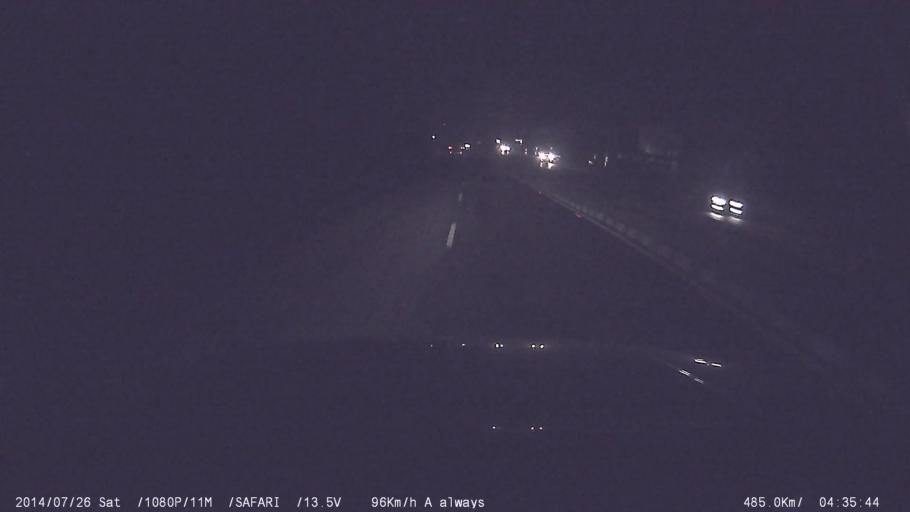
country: IN
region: Kerala
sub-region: Thrissur District
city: Kizhake Chalakudi
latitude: 10.2658
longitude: 76.3516
